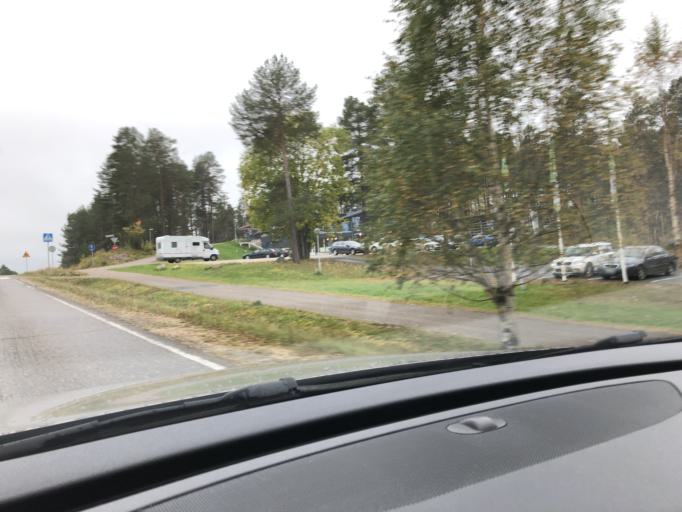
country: FI
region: Lapland
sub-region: Itae-Lappi
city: Posio
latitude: 66.1130
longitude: 28.1812
